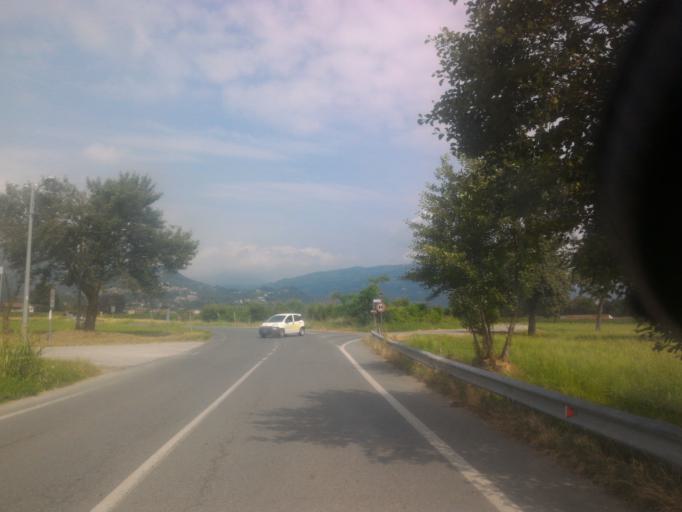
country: IT
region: Piedmont
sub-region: Provincia di Torino
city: San Secondo di Pinerolo
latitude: 44.8589
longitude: 7.3208
